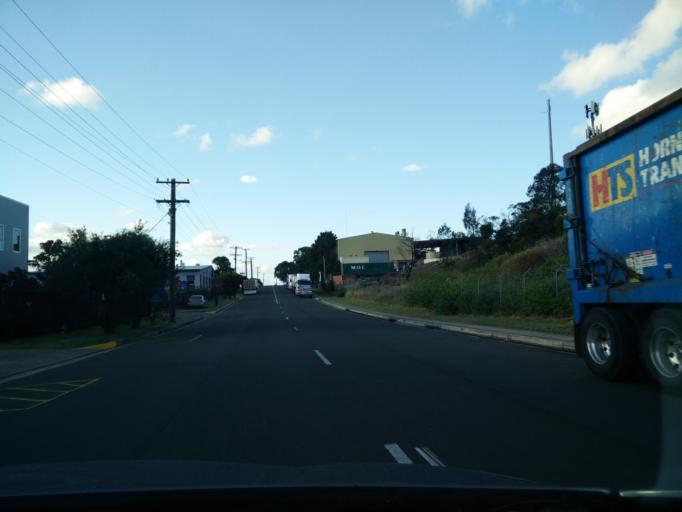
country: AU
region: New South Wales
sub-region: Wollongong
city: Cordeaux Heights
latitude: -34.4609
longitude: 150.8442
